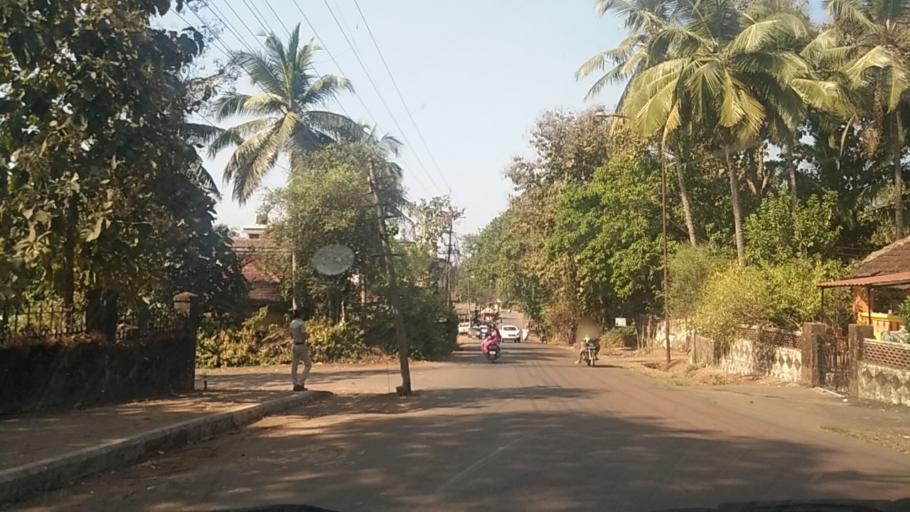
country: IN
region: Goa
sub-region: South Goa
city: Sanguem
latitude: 15.2282
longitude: 74.1537
